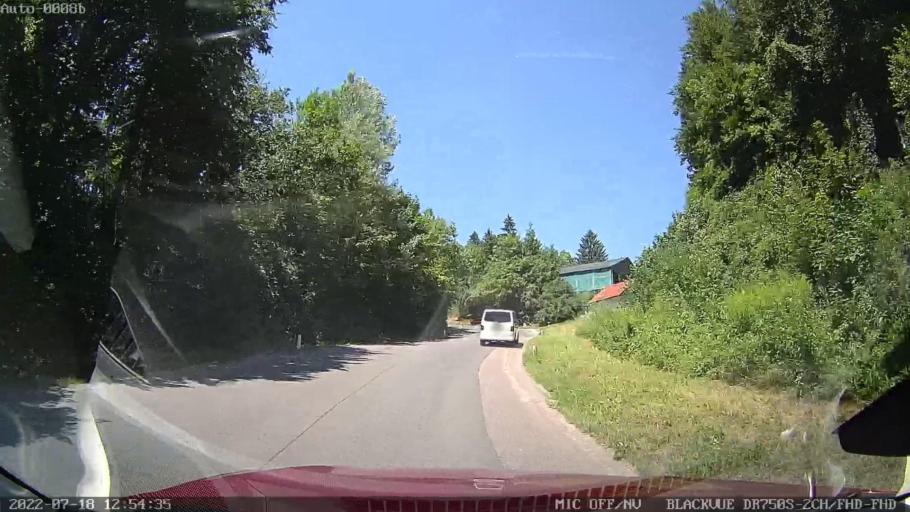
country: SI
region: Dobrova-Horjul-Polhov Gradec
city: Dobrova
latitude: 46.0757
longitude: 14.4408
